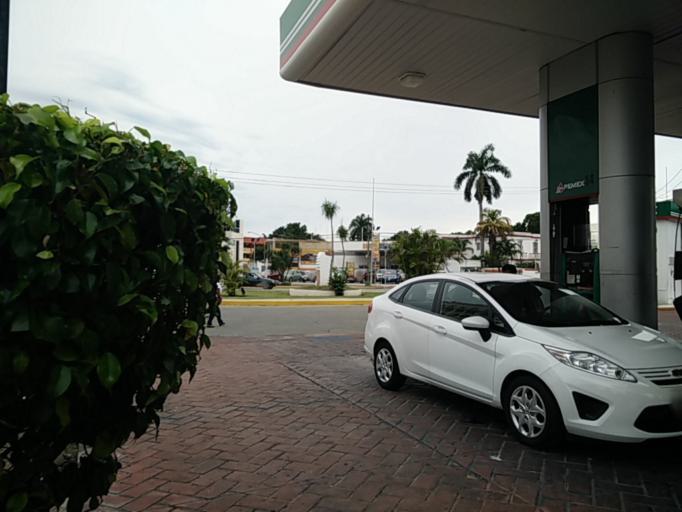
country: MX
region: Yucatan
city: Merida
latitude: 20.9877
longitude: -89.6192
